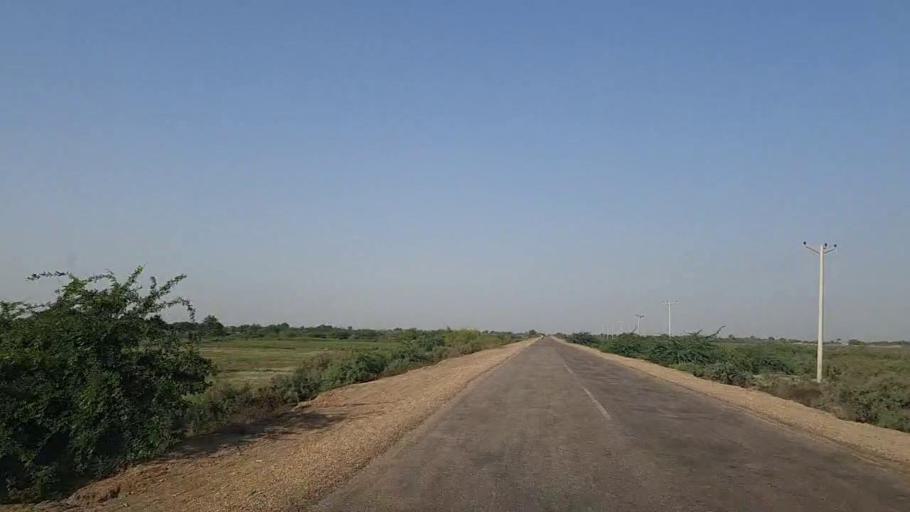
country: PK
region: Sindh
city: Mirpur Batoro
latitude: 24.6150
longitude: 68.4046
